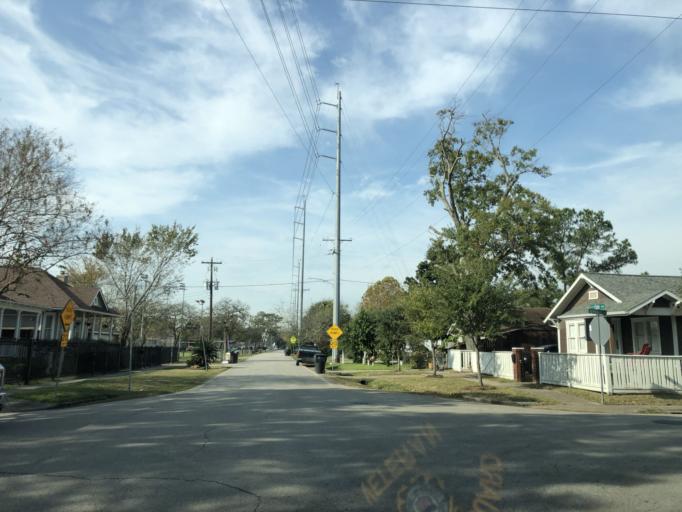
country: US
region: Texas
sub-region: Harris County
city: Houston
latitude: 29.7943
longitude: -95.4061
